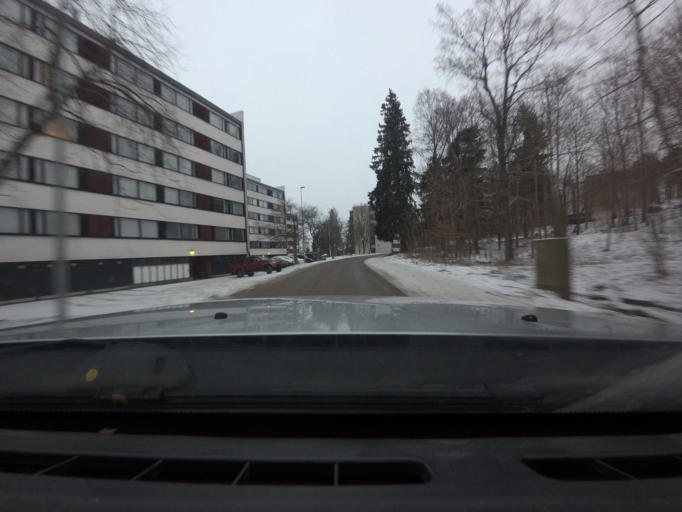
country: FI
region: Uusimaa
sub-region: Helsinki
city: Kauniainen
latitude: 60.2295
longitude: 24.7331
